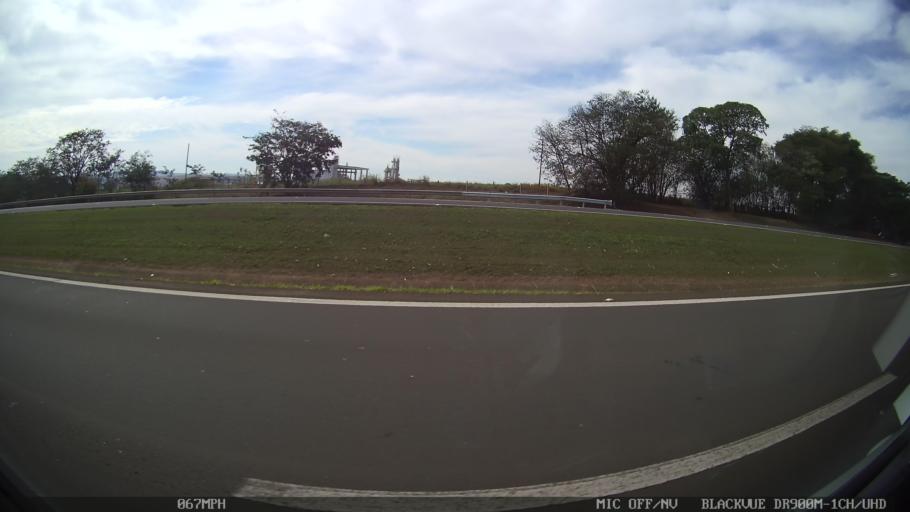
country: BR
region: Sao Paulo
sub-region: Matao
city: Matao
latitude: -21.5932
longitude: -48.4401
